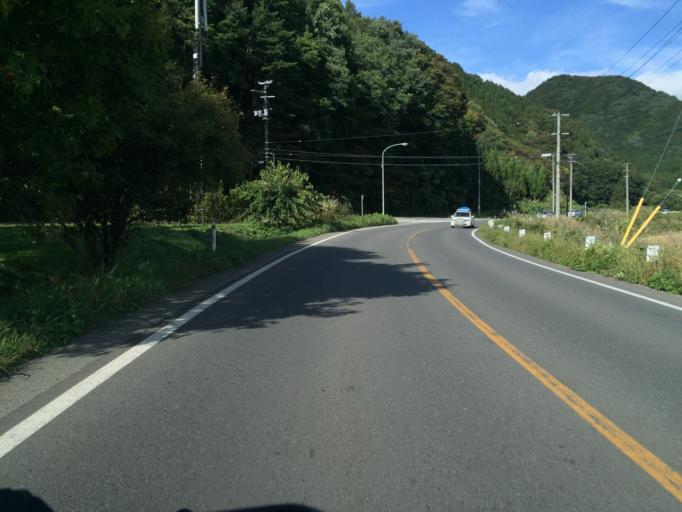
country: JP
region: Fukushima
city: Inawashiro
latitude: 37.6193
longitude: 140.1461
